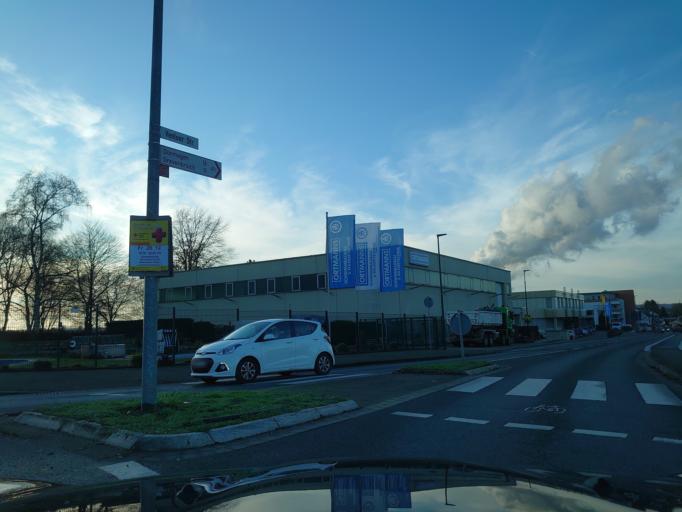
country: DE
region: North Rhine-Westphalia
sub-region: Regierungsbezirk Dusseldorf
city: Rommerskirchen
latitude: 51.0331
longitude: 6.6931
